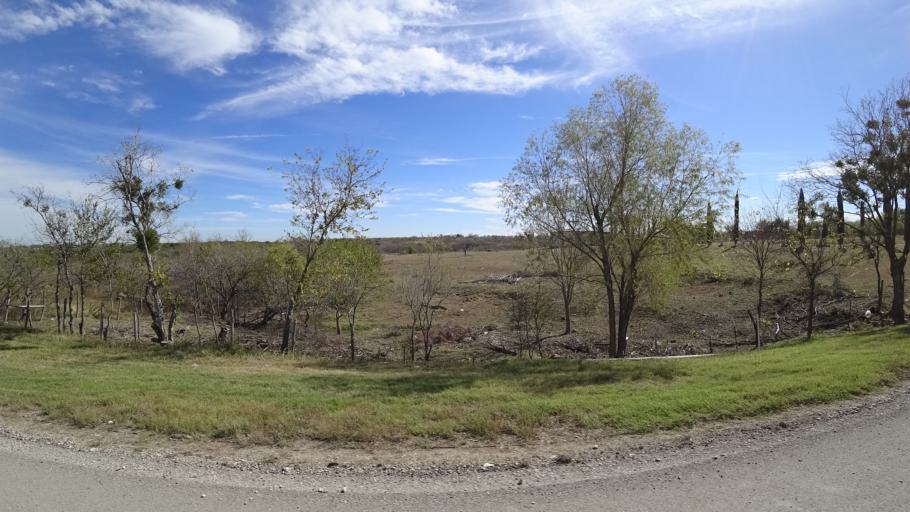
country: US
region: Texas
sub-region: Travis County
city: Onion Creek
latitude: 30.1207
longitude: -97.6899
